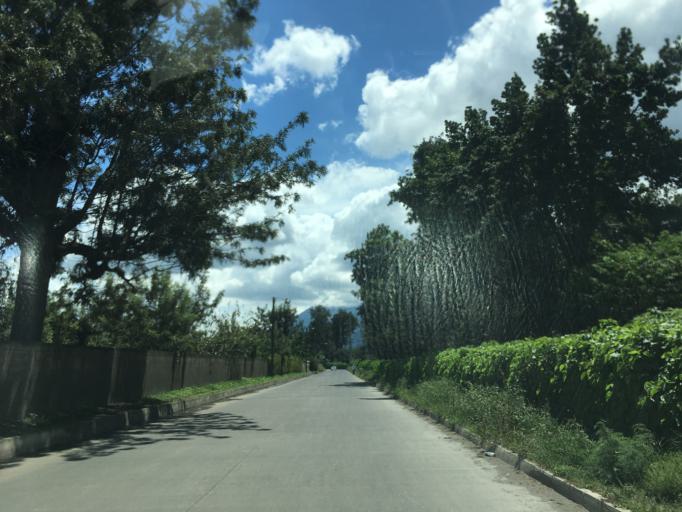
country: GT
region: Sacatepequez
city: Antigua Guatemala
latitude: 14.5441
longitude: -90.7336
